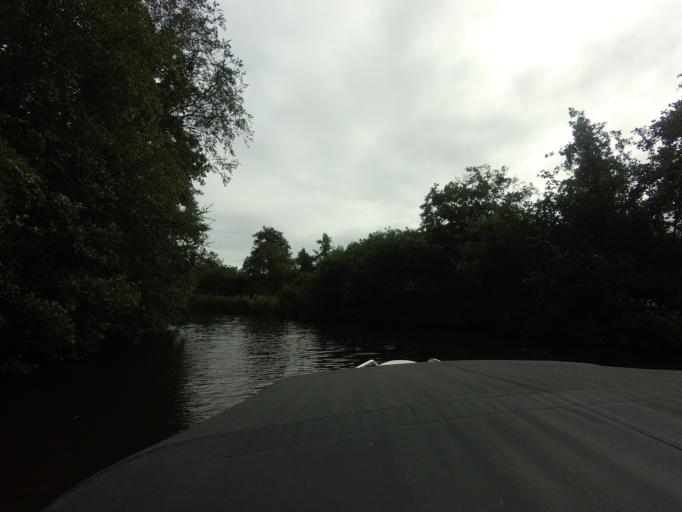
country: NL
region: Friesland
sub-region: Gemeente Boarnsterhim
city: Warten
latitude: 53.1268
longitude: 5.9050
